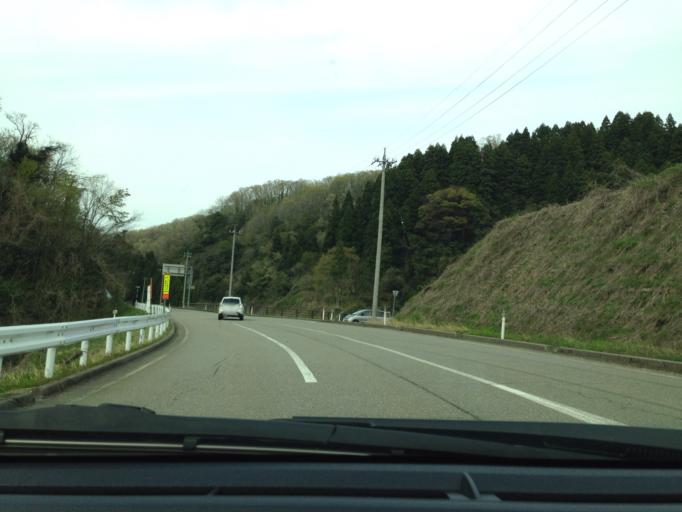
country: JP
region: Ishikawa
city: Kanazawa-shi
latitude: 36.5497
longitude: 136.7309
